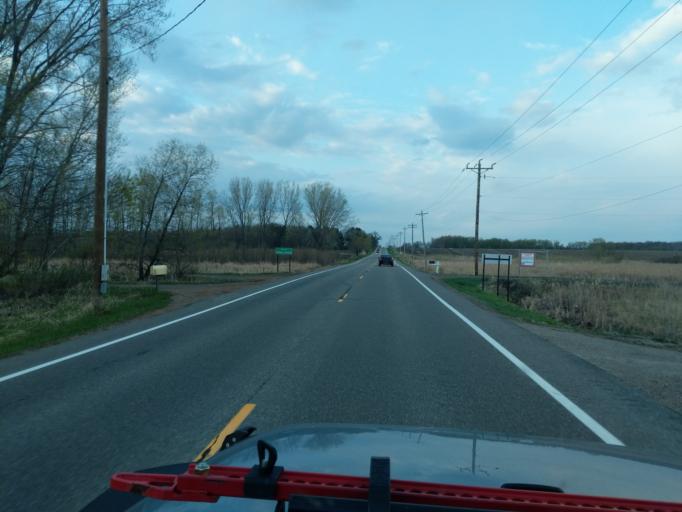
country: US
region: Minnesota
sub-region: Hennepin County
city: Rogers
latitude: 45.1533
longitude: -93.5219
